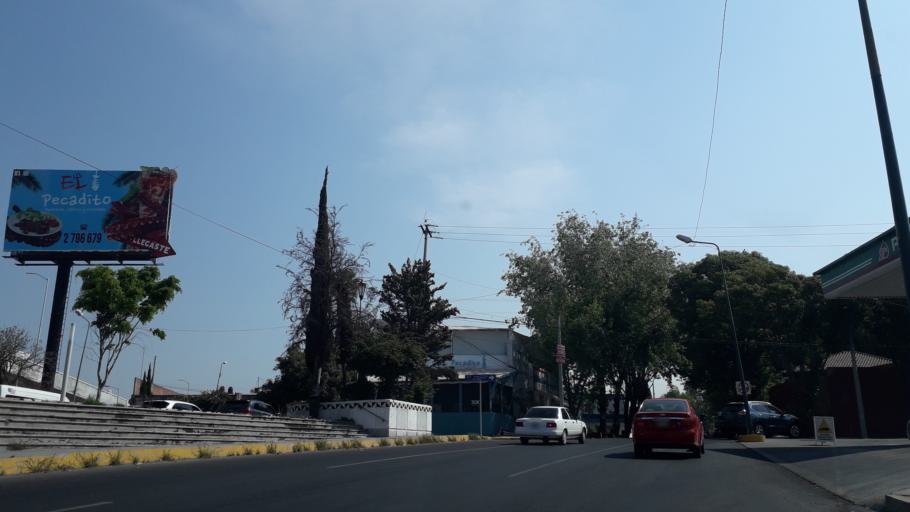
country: MX
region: Puebla
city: Puebla
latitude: 19.0377
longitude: -98.2252
